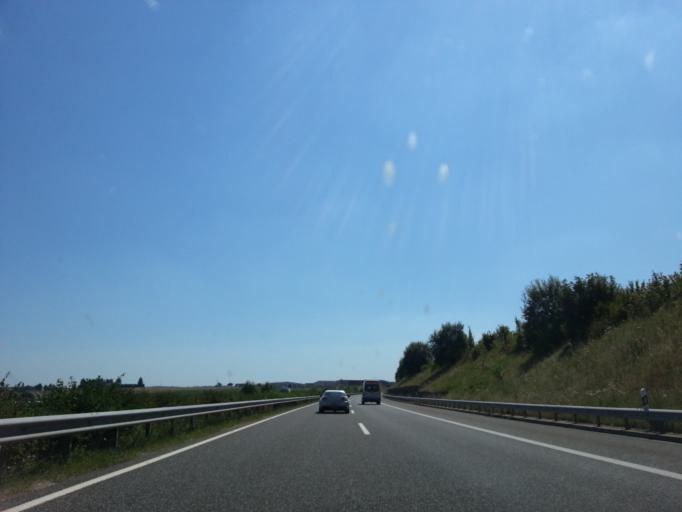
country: DE
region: Rheinland-Pfalz
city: Landscheid
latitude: 49.9958
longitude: 6.7712
